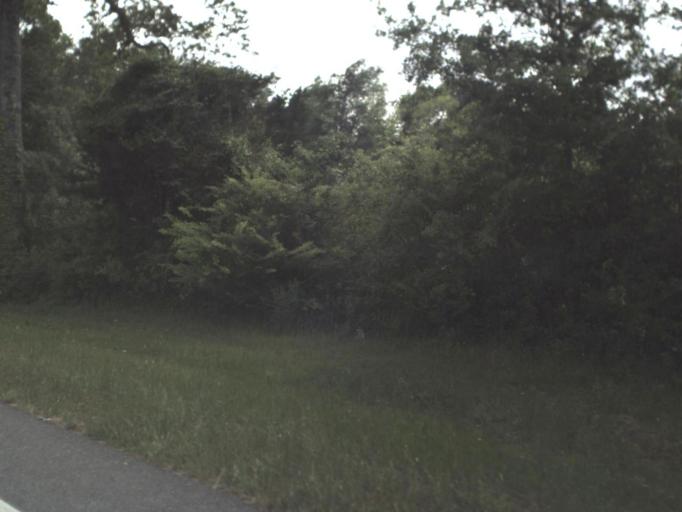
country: US
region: Alabama
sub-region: Escambia County
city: East Brewton
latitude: 30.9833
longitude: -87.0427
